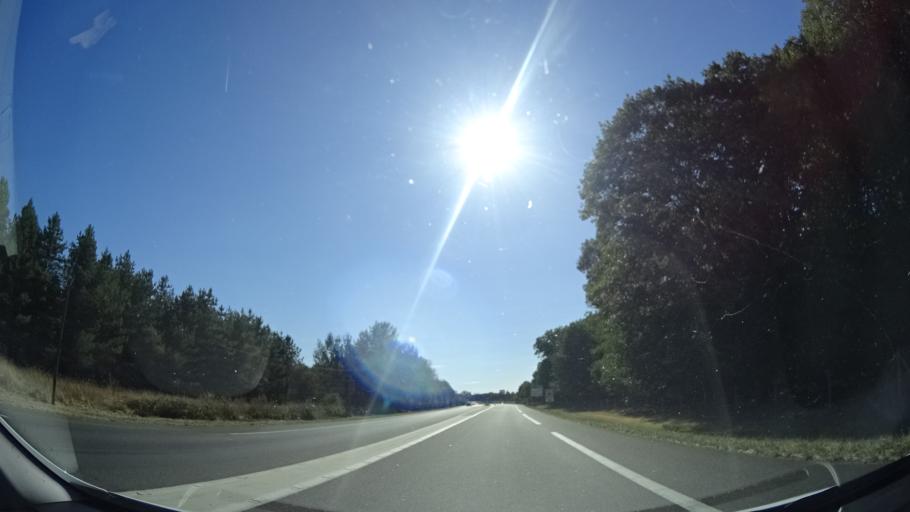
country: FR
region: Centre
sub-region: Departement du Loiret
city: Chateauneuf-sur-Loire
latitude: 47.8849
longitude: 2.2442
